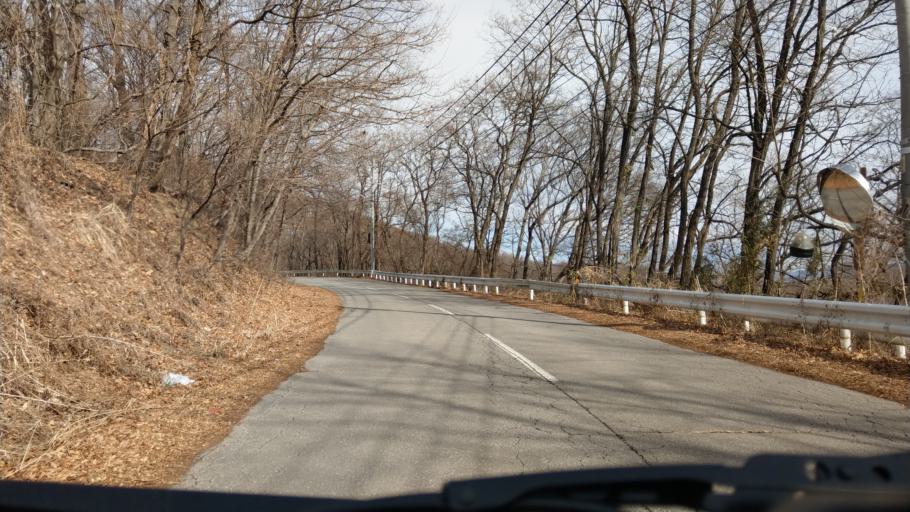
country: JP
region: Nagano
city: Komoro
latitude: 36.2835
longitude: 138.4053
